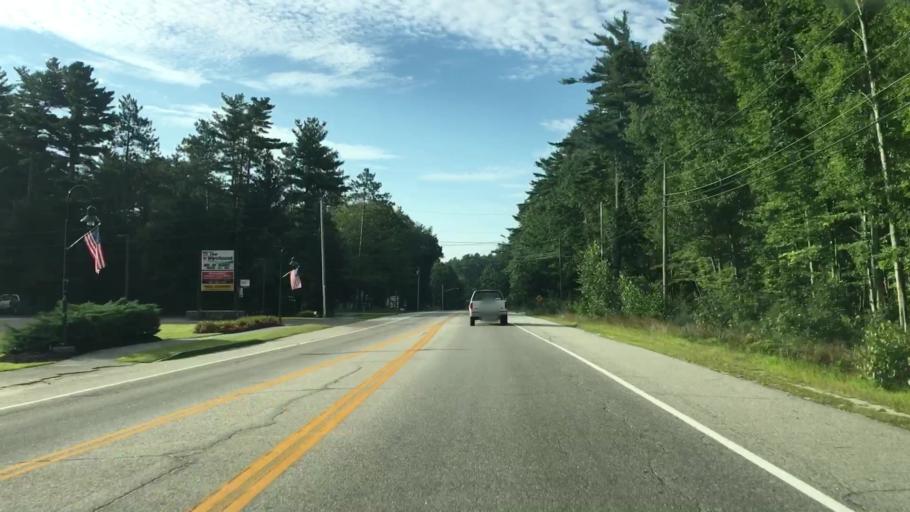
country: US
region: Maine
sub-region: Cumberland County
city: Raymond
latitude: 43.8785
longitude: -70.4656
